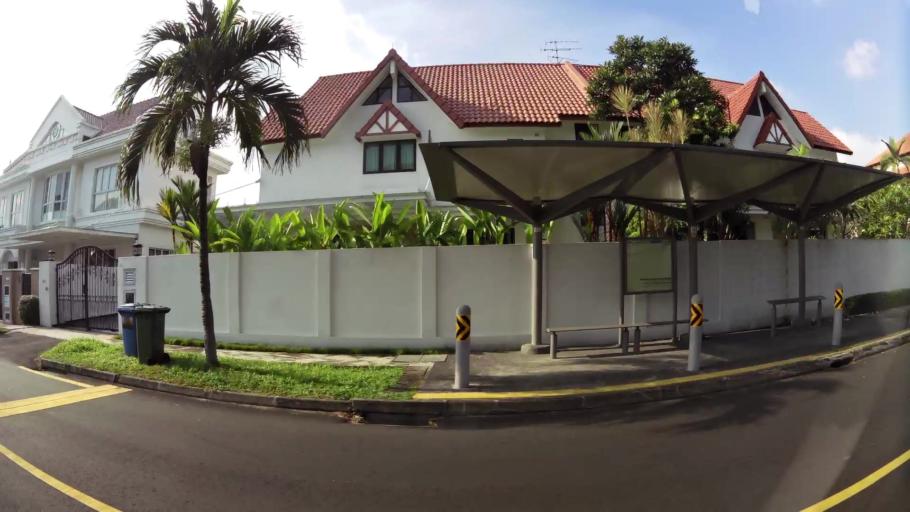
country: SG
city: Singapore
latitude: 1.3173
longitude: 103.9160
